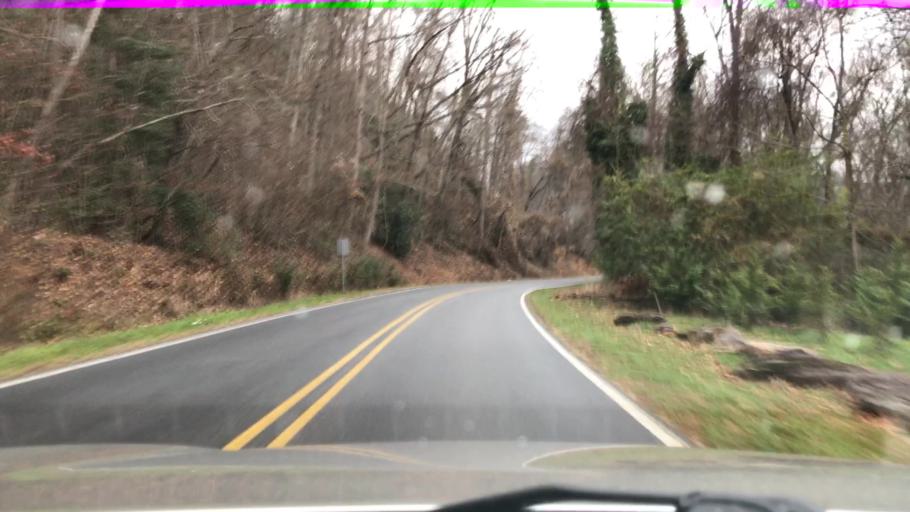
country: US
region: North Carolina
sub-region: Buncombe County
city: Avery Creek
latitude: 35.4769
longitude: -82.5578
